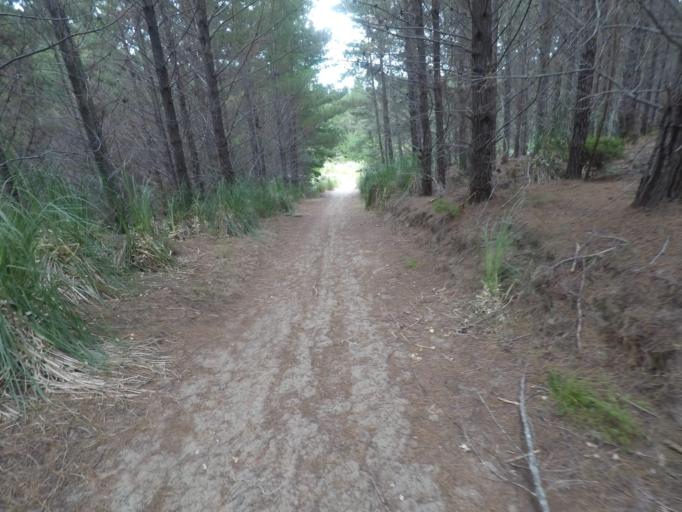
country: NZ
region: Auckland
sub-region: Auckland
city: Parakai
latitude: -36.6012
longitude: 174.2825
